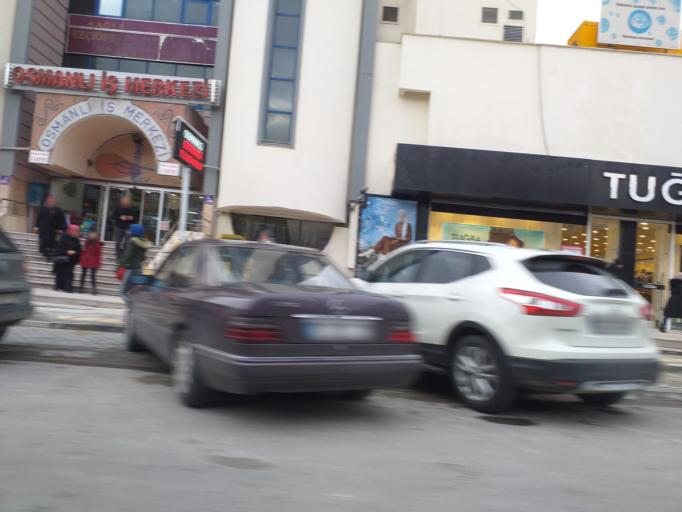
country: TR
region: Ankara
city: Ankara
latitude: 39.9738
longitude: 32.8302
